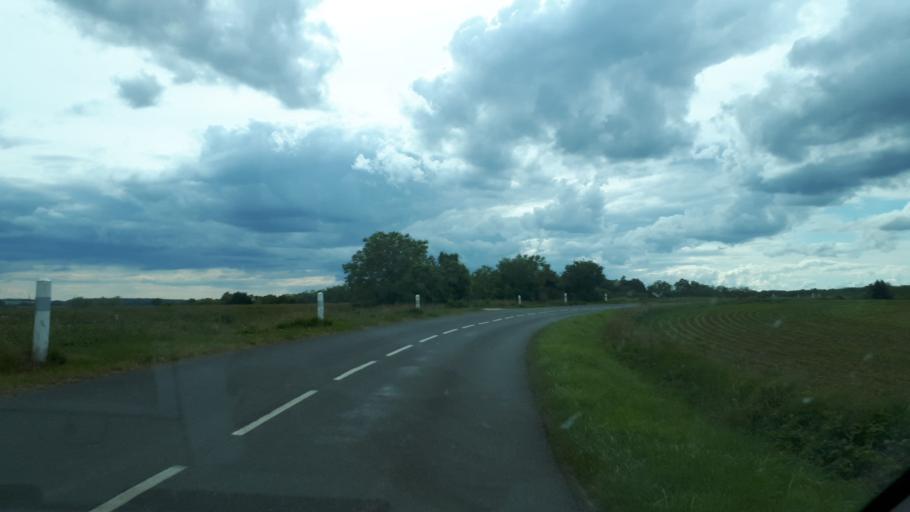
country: FR
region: Centre
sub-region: Departement du Cher
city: Gracay
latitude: 47.1352
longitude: 1.8822
